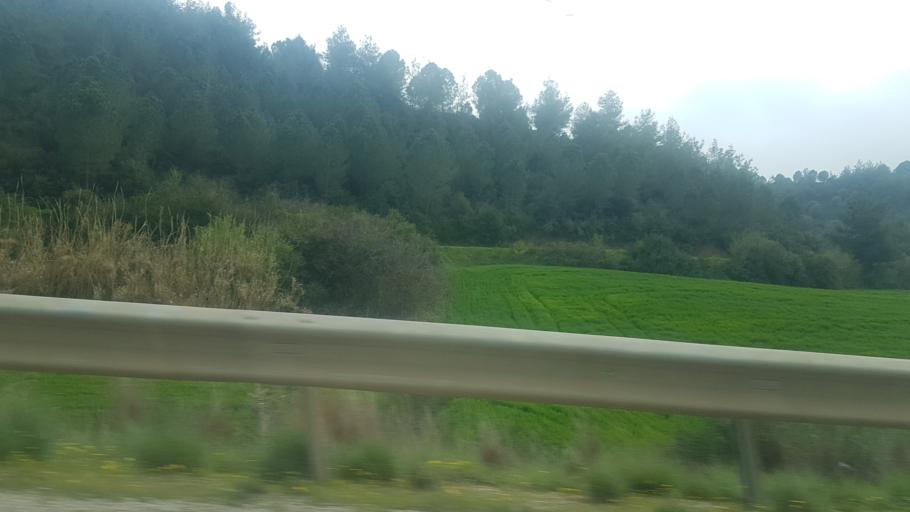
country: TR
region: Mersin
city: Yenice
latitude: 37.0898
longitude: 35.1537
